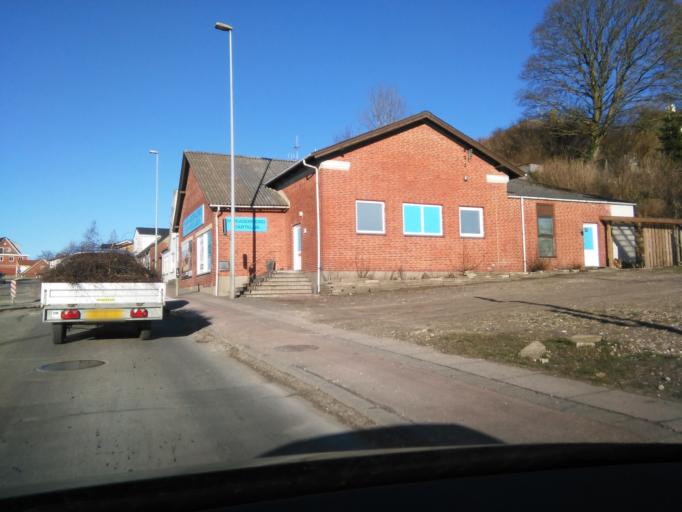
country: DK
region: North Denmark
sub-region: Mariagerfjord Kommune
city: Hobro
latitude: 56.6429
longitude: 9.7930
